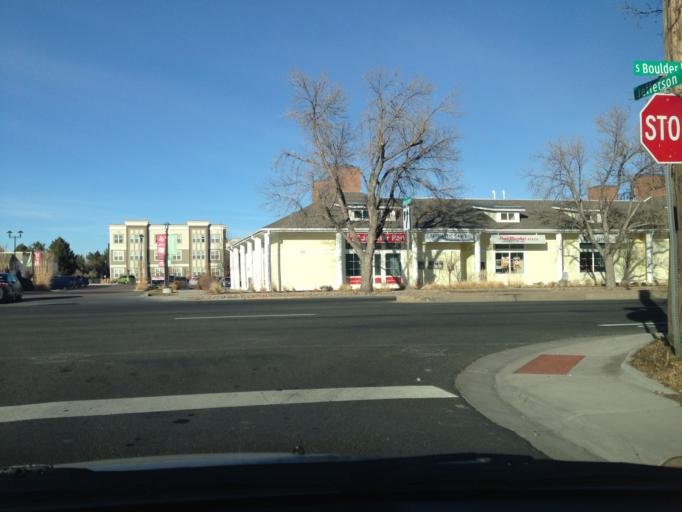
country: US
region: Colorado
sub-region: Boulder County
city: Louisville
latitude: 39.9867
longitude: -105.1349
